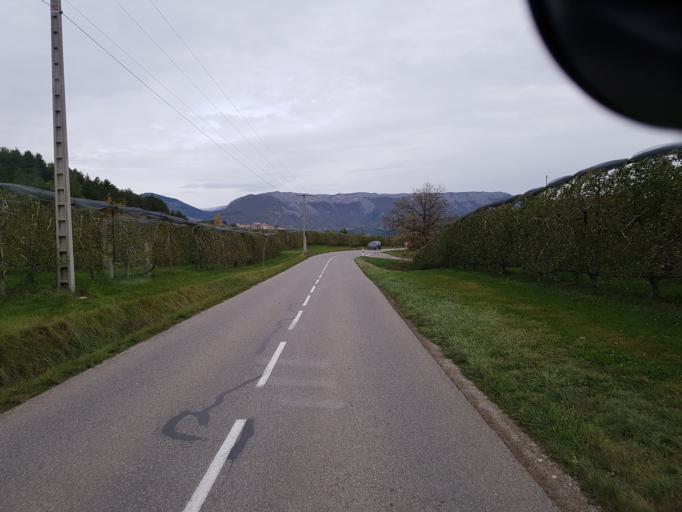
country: FR
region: Provence-Alpes-Cote d'Azur
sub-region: Departement des Hautes-Alpes
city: Laragne-Monteglin
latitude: 44.3299
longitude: 5.7480
